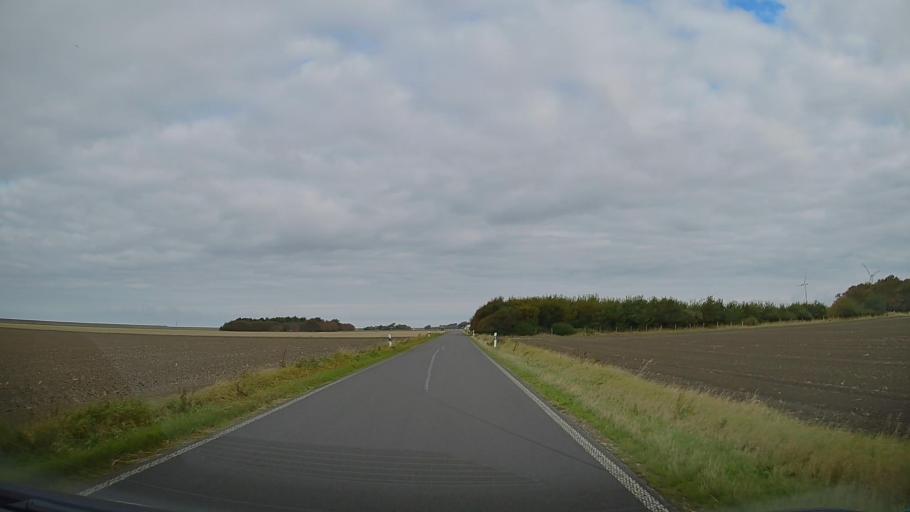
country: DE
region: Schleswig-Holstein
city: Friedrich-Wilhelm-Lubke-Koog
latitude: 54.8648
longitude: 8.6253
